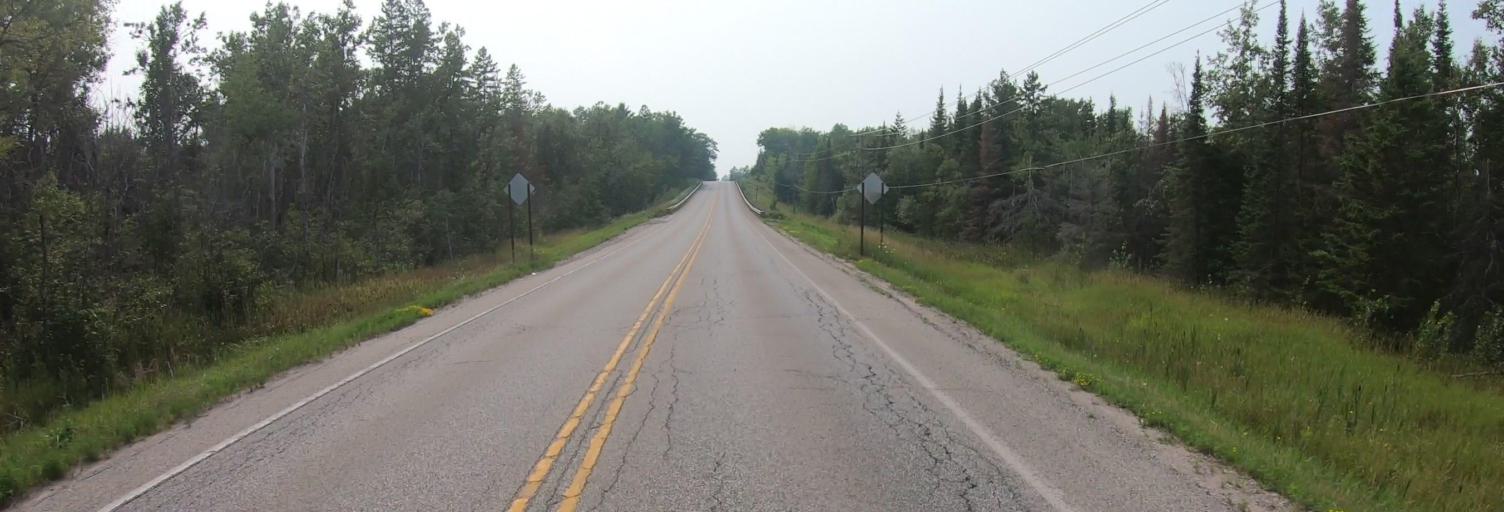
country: US
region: Michigan
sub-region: Chippewa County
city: Sault Ste. Marie
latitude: 46.4629
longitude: -84.3243
